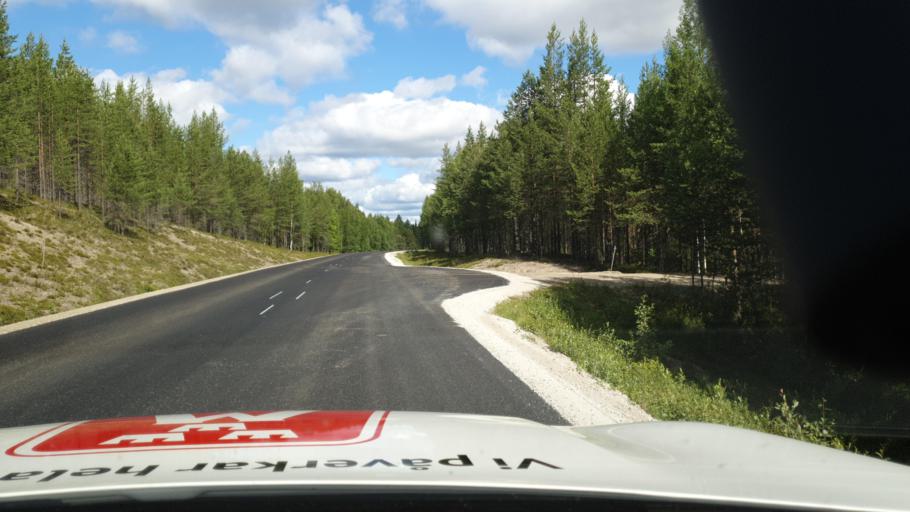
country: SE
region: Vaesterbotten
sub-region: Lycksele Kommun
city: Lycksele
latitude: 64.8425
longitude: 18.7645
